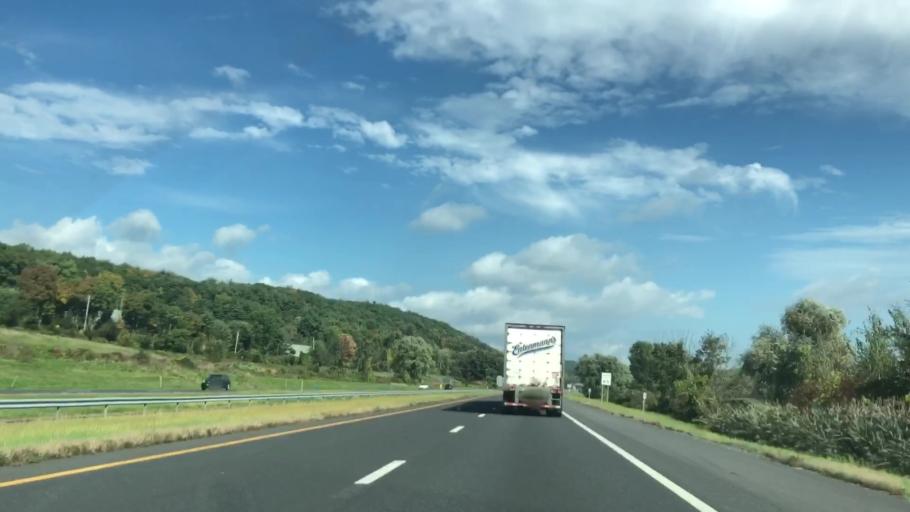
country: US
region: New York
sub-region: Ulster County
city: Lincoln Park
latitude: 41.9618
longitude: -74.0151
